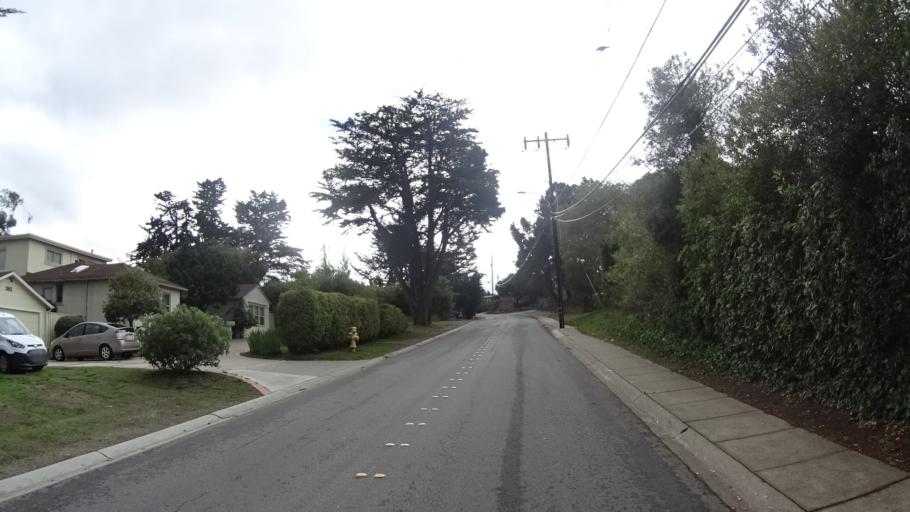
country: US
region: California
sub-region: San Mateo County
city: San Bruno
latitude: 37.6422
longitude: -122.4339
